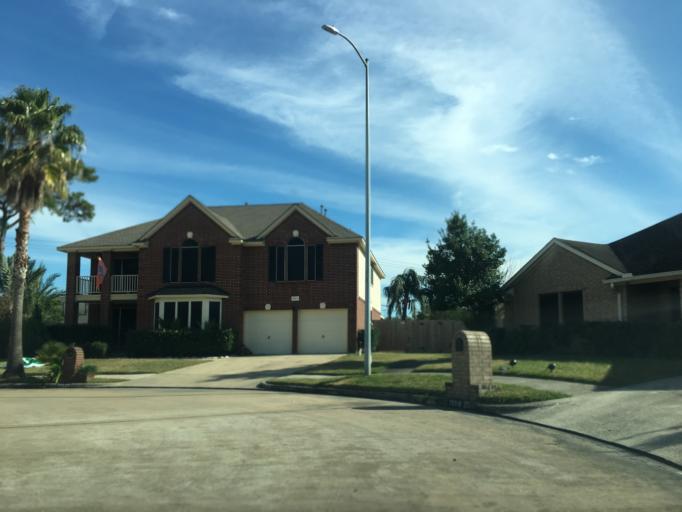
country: US
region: Texas
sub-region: Harris County
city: Cloverleaf
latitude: 29.8089
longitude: -95.1680
